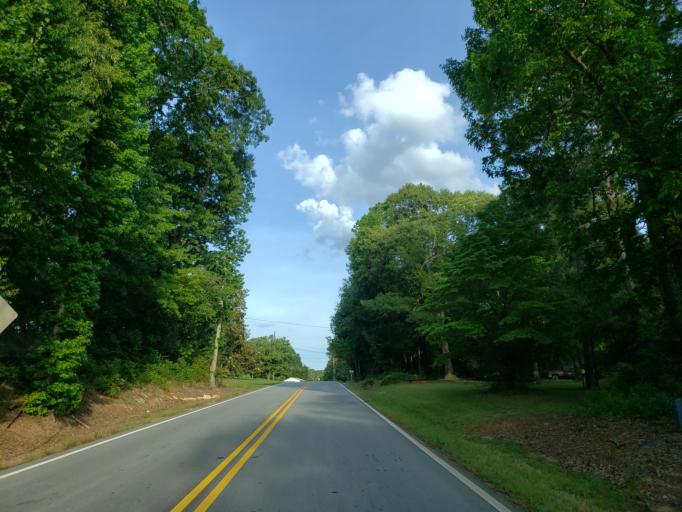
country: US
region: Georgia
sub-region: Carroll County
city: Mount Zion
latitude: 33.6368
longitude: -85.1921
